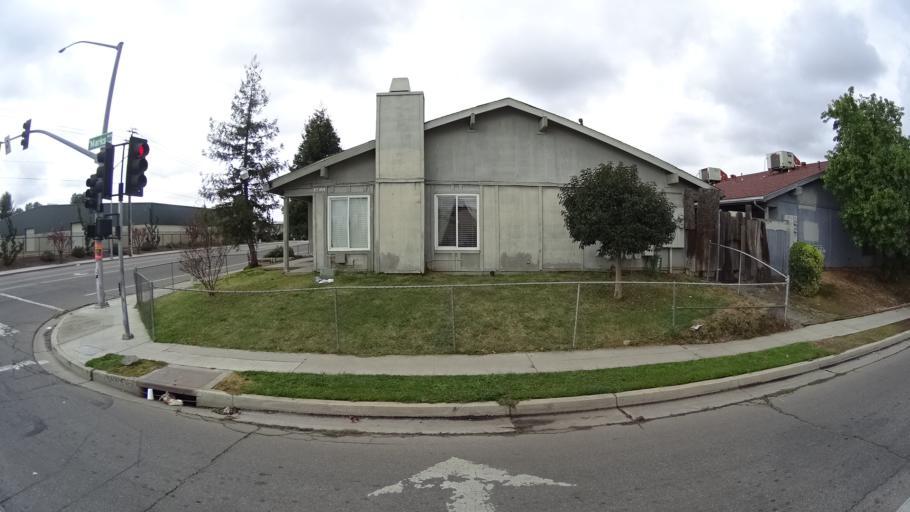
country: US
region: California
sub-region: Fresno County
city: West Park
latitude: 36.7867
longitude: -119.8444
